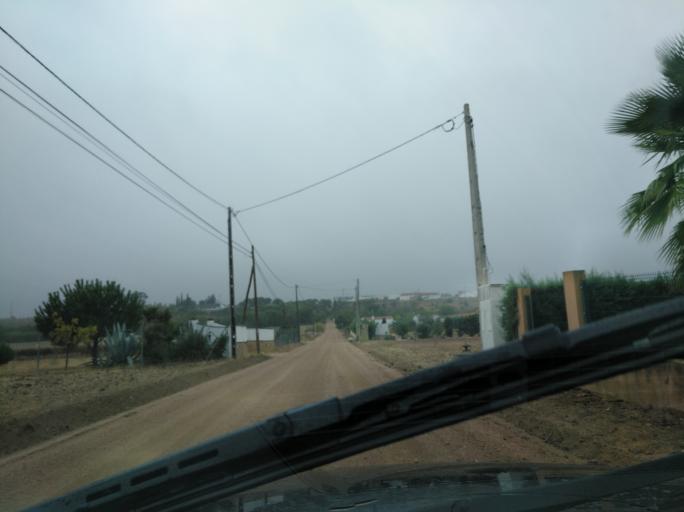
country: PT
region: Portalegre
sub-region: Campo Maior
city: Campo Maior
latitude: 38.9550
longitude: -7.0714
